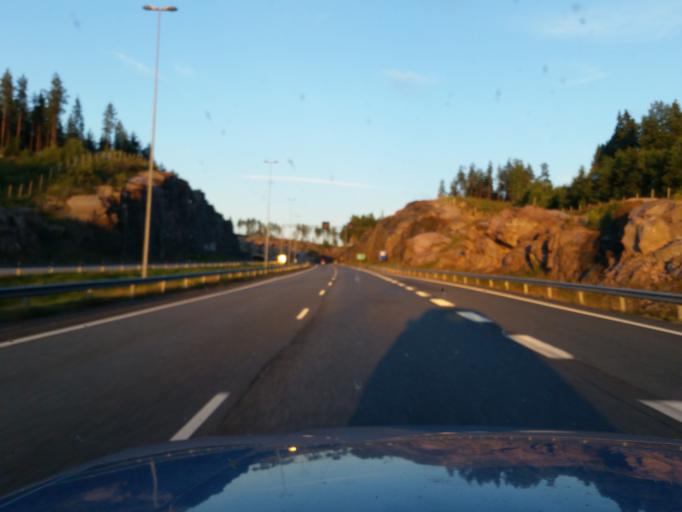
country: FI
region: Varsinais-Suomi
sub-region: Salo
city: Muurla
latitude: 60.3780
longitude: 23.3250
